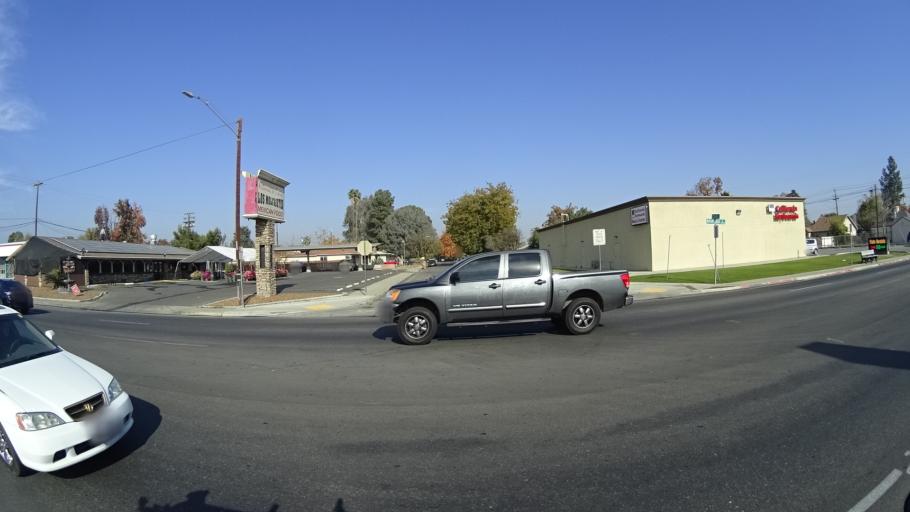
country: US
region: California
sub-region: Kern County
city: Bakersfield
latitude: 35.3540
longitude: -119.0306
